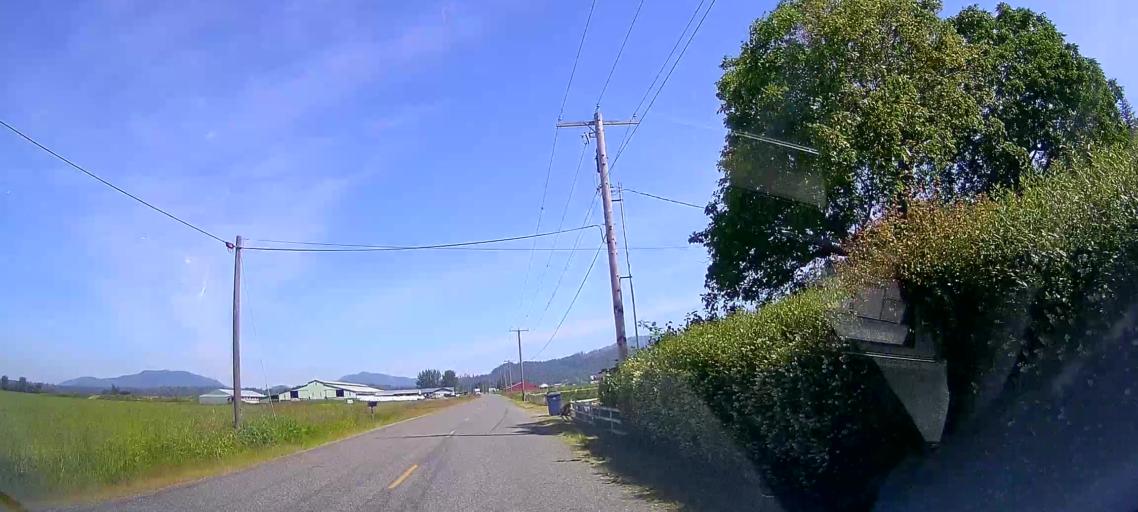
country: US
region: Washington
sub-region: Skagit County
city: Burlington
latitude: 48.4976
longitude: -122.3076
